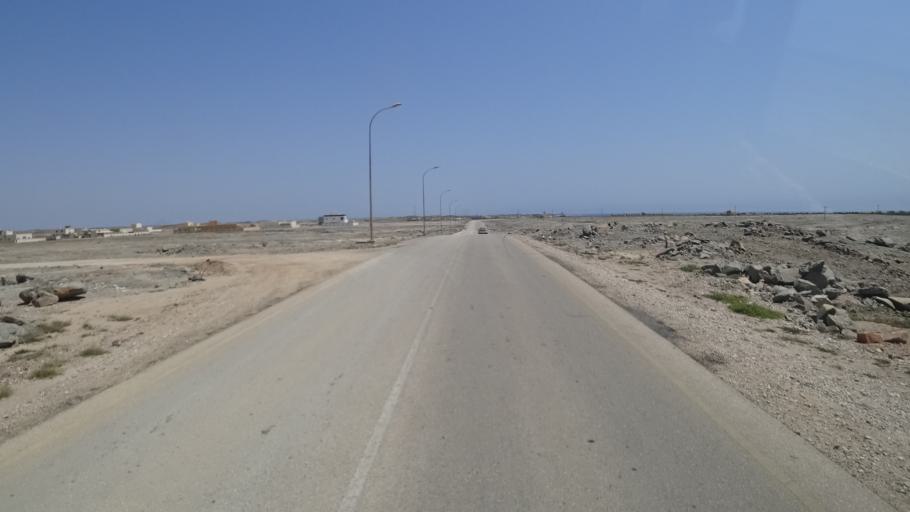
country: OM
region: Zufar
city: Salalah
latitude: 16.9677
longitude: 54.7326
